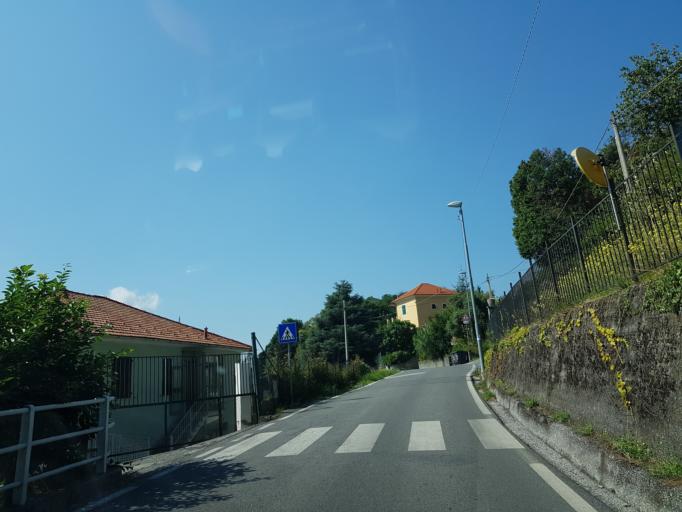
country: IT
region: Liguria
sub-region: Provincia di Genova
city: Pedemonte
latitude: 44.4923
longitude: 8.9131
